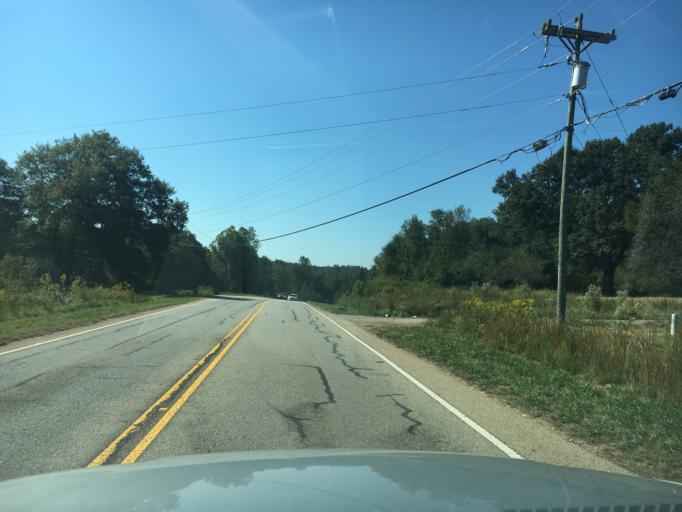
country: US
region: South Carolina
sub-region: Greenville County
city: Taylors
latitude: 34.9092
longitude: -82.2735
